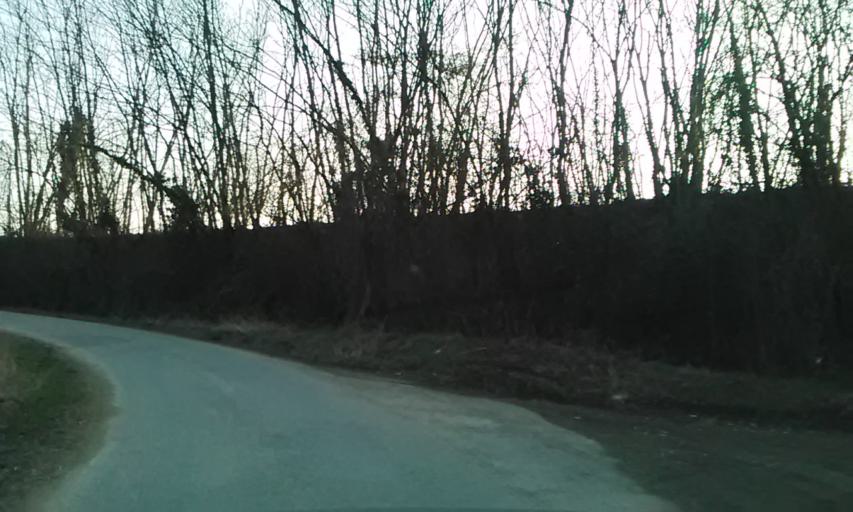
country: IT
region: Piedmont
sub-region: Provincia di Biella
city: Cavaglia
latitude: 45.4087
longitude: 8.1158
